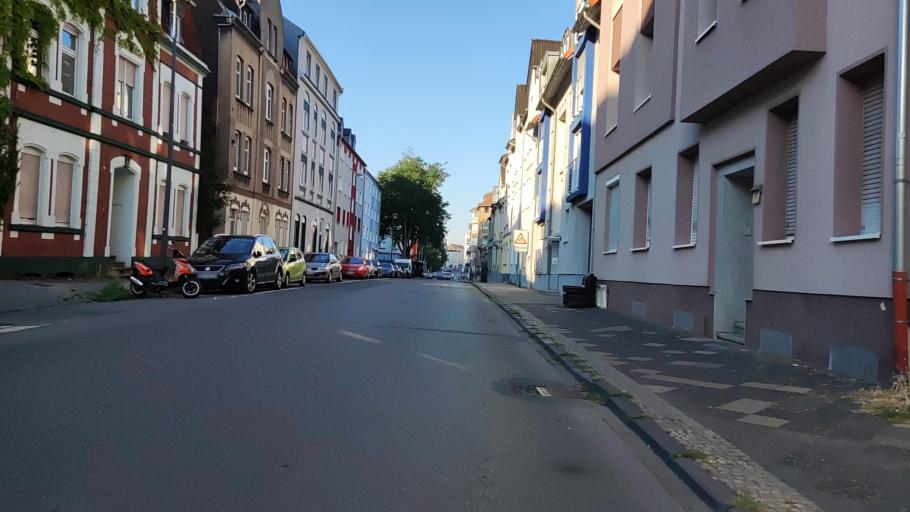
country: DE
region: North Rhine-Westphalia
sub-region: Regierungsbezirk Arnsberg
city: Herne
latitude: 51.5405
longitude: 7.2344
